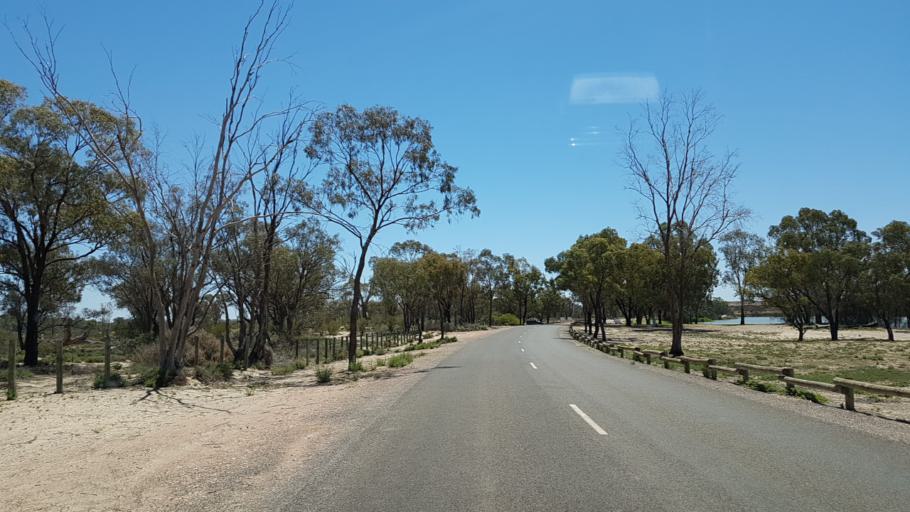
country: AU
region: South Australia
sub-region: Loxton Waikerie
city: Waikerie
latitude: -34.1701
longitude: 139.9768
